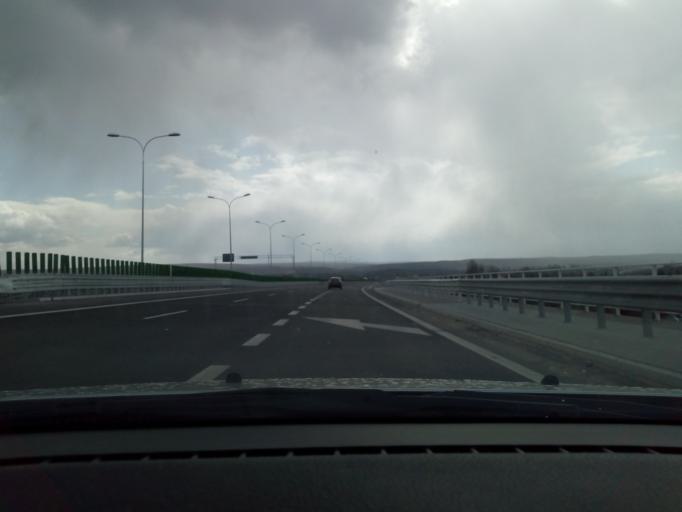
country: PL
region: Swietokrzyskie
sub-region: Powiat skarzyski
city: Skarzysko-Kamienna
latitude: 51.1190
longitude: 20.8473
